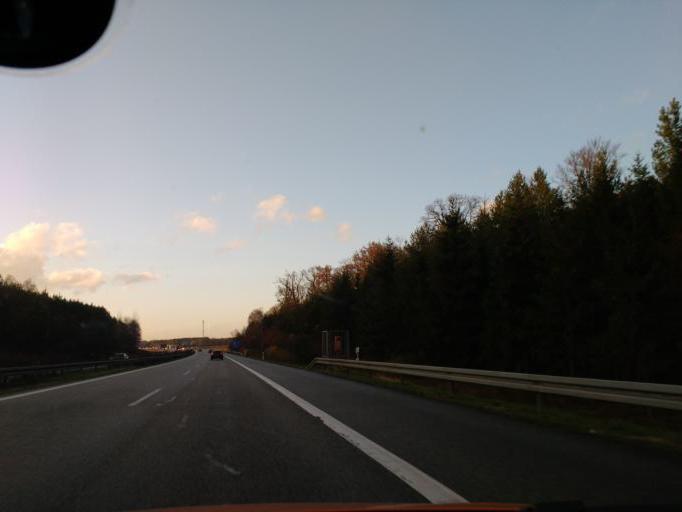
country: DE
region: Mecklenburg-Vorpommern
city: Sulstorf
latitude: 53.4805
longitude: 11.2907
